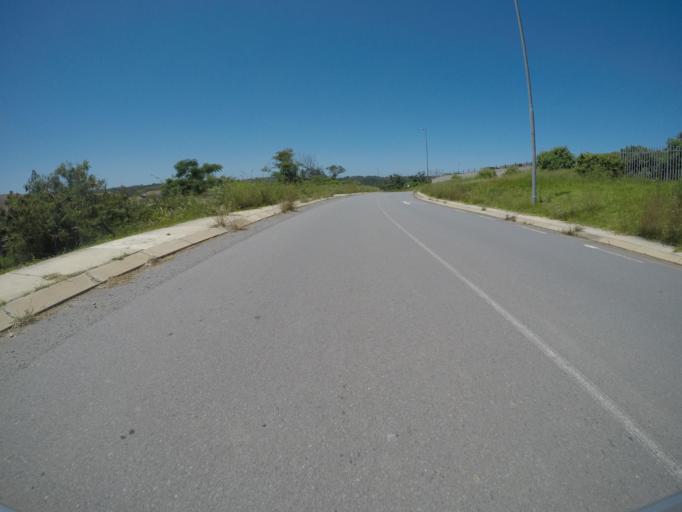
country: ZA
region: Eastern Cape
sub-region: Buffalo City Metropolitan Municipality
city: East London
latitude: -32.9532
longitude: 27.9464
